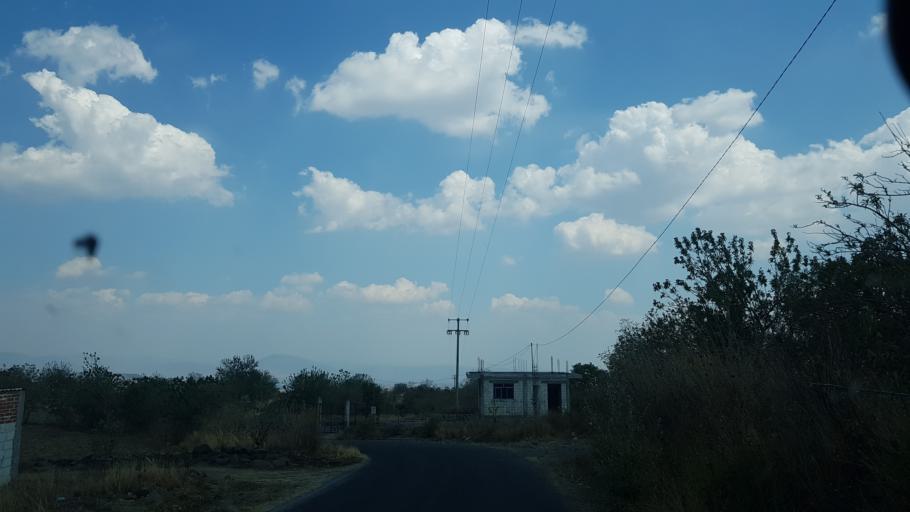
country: MX
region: Puebla
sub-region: Atlixco
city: San Pedro Benito Juarez
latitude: 18.9491
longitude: -98.5407
